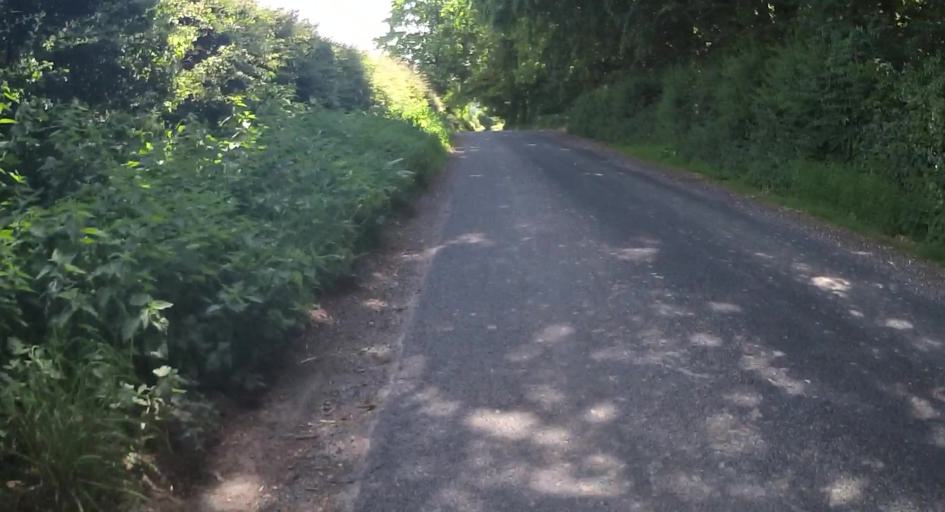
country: GB
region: England
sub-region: Hampshire
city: Kingsclere
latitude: 51.3208
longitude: -1.2943
